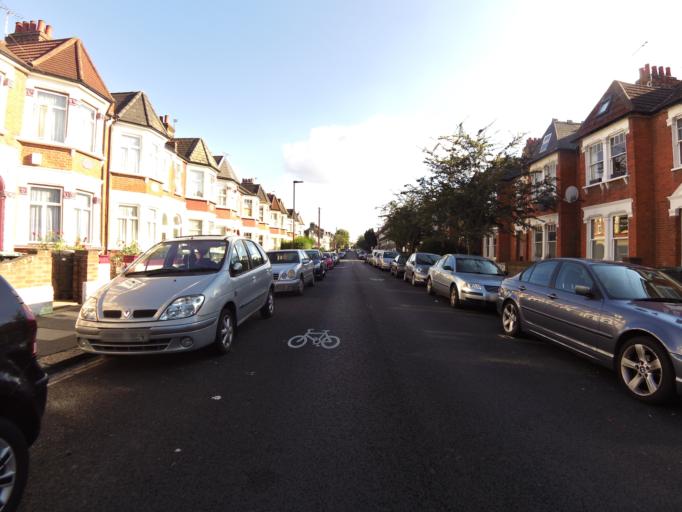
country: GB
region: England
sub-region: Greater London
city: Harringay
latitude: 51.5977
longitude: -0.0760
